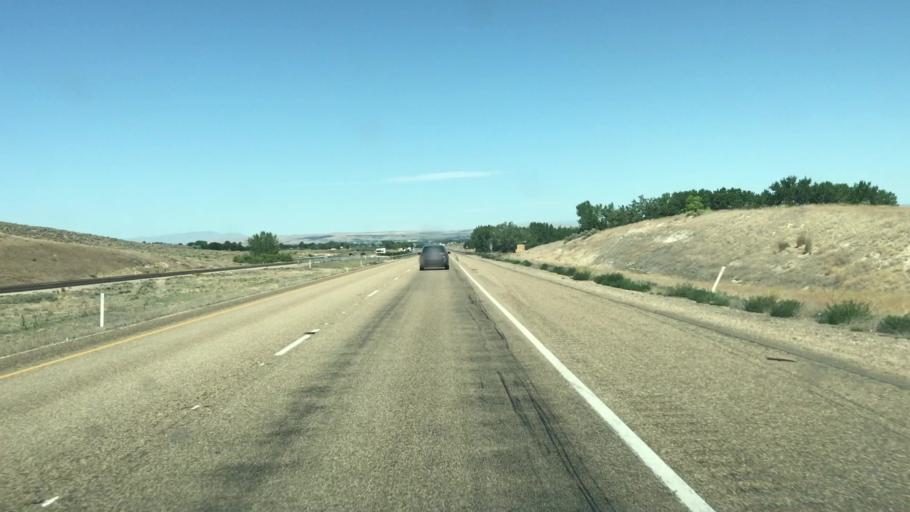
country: US
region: Idaho
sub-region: Payette County
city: New Plymouth
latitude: 43.9400
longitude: -116.8646
